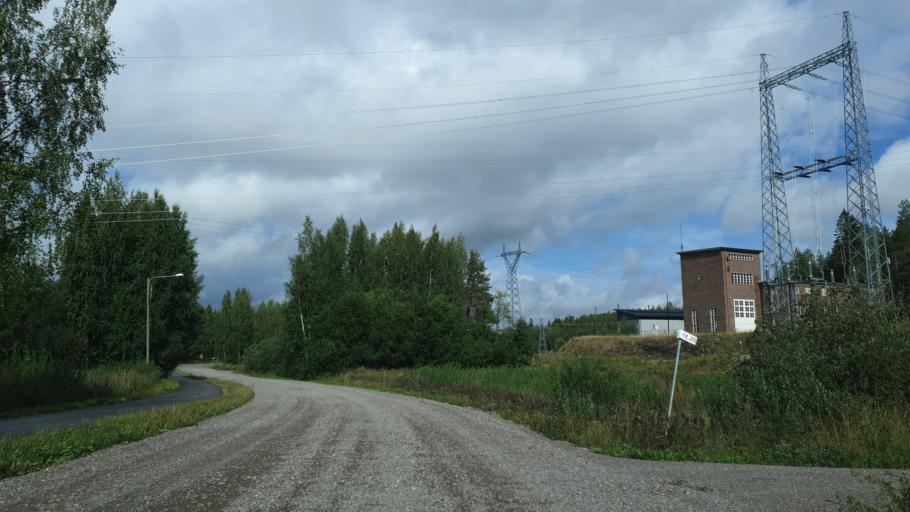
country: FI
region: Northern Savo
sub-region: Varkaus
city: Varkaus
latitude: 62.3385
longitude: 27.8550
